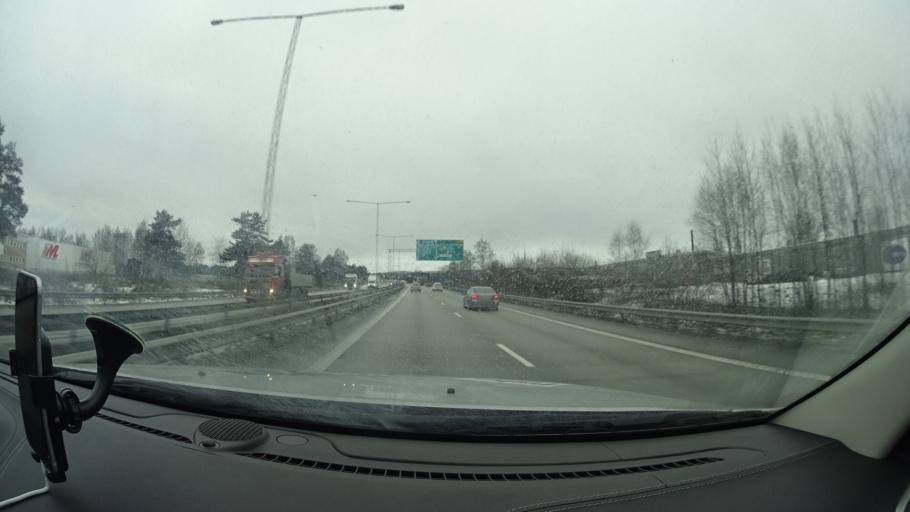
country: SE
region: Joenkoeping
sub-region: Jonkopings Kommun
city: Jonkoping
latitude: 57.7593
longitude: 14.1679
